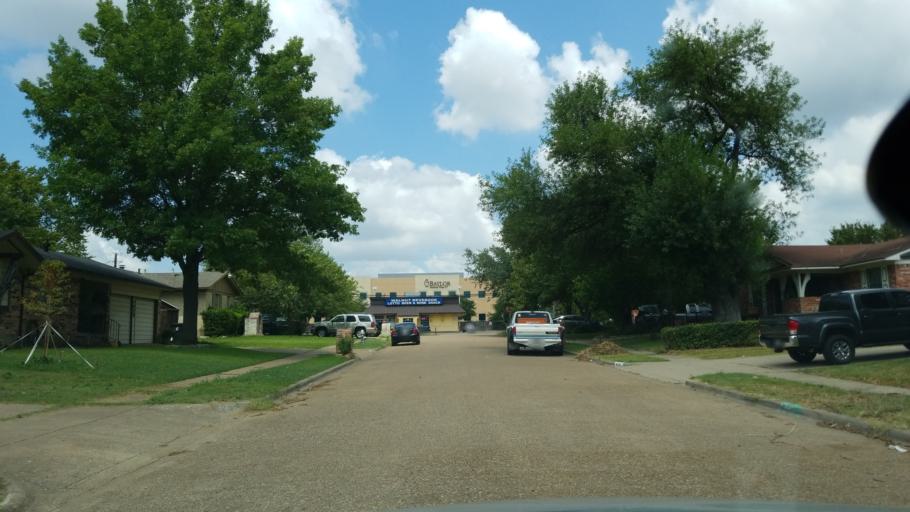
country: US
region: Texas
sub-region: Dallas County
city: Garland
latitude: 32.9156
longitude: -96.6610
